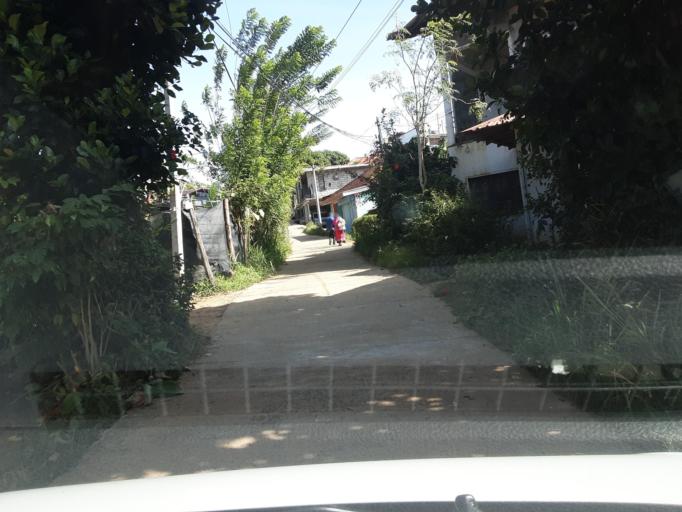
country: LK
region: Uva
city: Haputale
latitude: 6.8938
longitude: 80.9207
